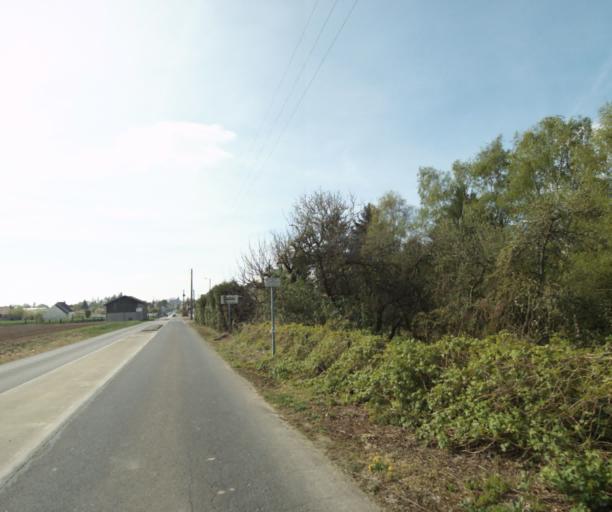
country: FR
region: Ile-de-France
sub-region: Departement de Seine-et-Marne
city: Nangis
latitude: 48.5663
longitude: 3.0127
